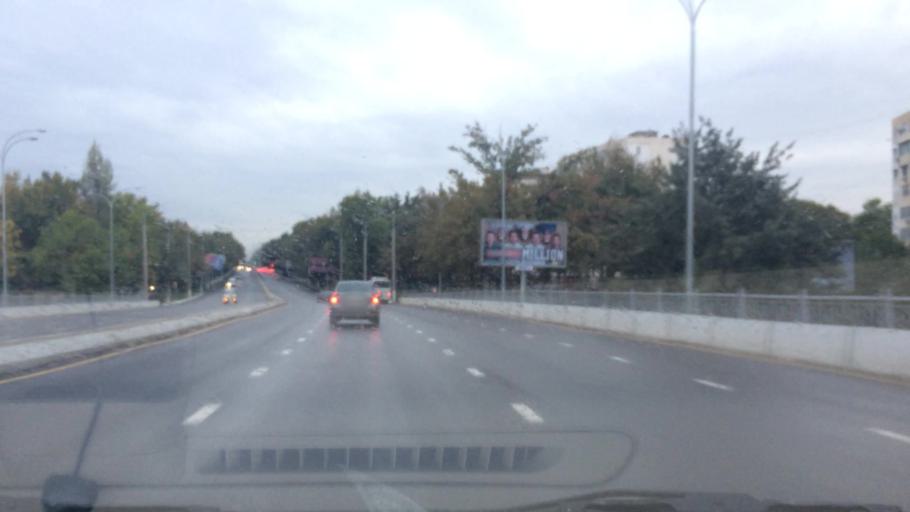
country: UZ
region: Toshkent Shahri
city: Tashkent
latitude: 41.2737
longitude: 69.2040
